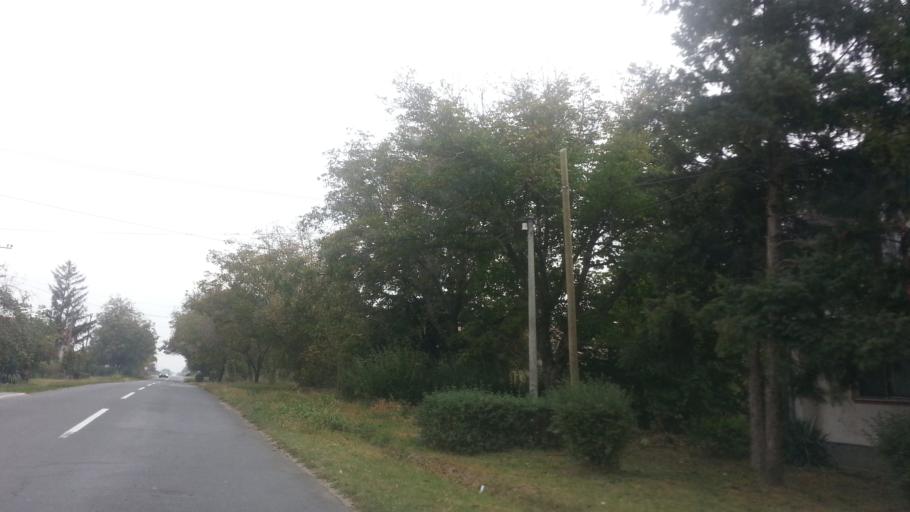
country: RS
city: Belegis
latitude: 45.0260
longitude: 20.3352
